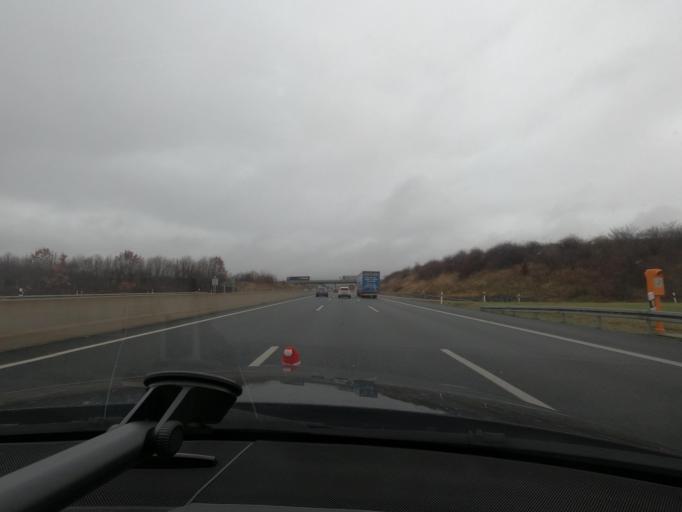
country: DE
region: Lower Saxony
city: Bockenem
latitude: 51.9975
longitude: 10.1562
